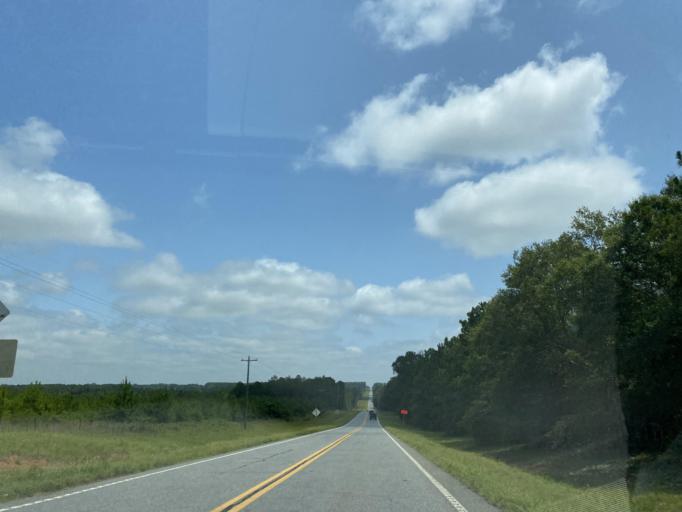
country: US
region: Georgia
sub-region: Telfair County
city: McRae
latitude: 32.0971
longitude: -82.8503
